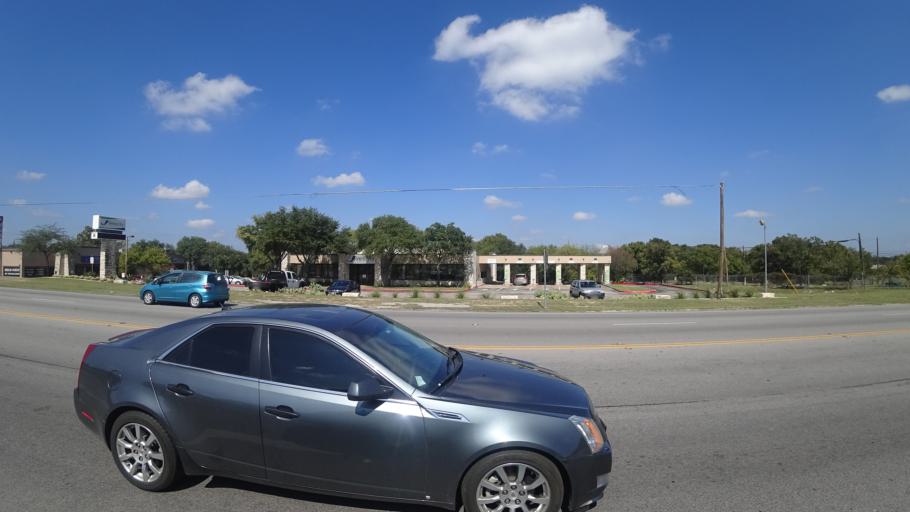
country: US
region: Texas
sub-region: Williamson County
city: Round Rock
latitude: 30.5114
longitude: -97.6902
